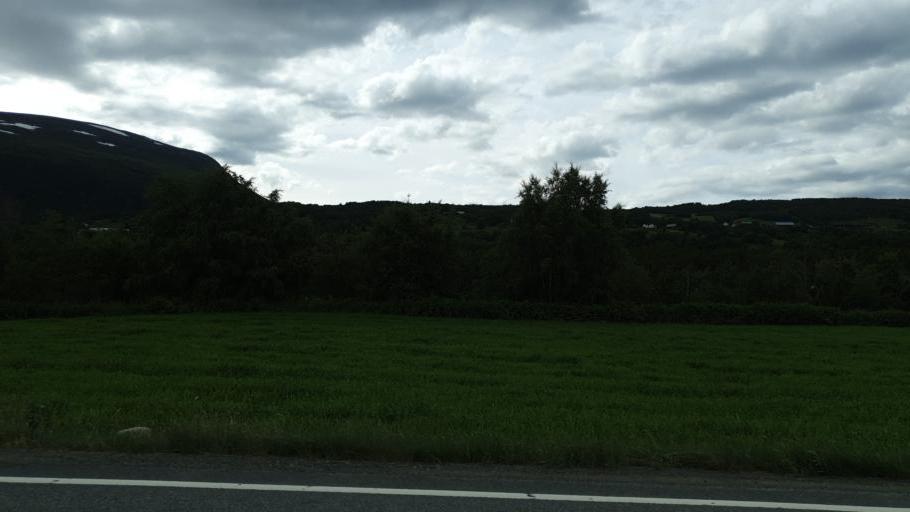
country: NO
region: Sor-Trondelag
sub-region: Oppdal
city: Oppdal
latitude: 62.5581
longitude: 9.6364
